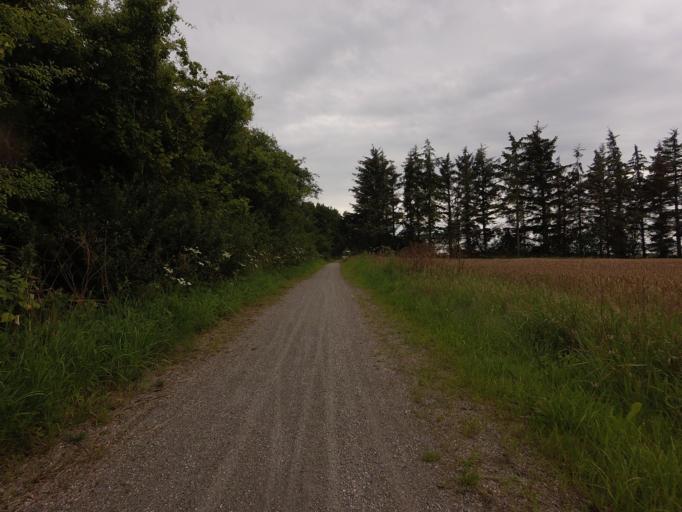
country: DK
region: North Denmark
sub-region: Alborg Kommune
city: Vadum
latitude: 57.1003
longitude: 9.8938
